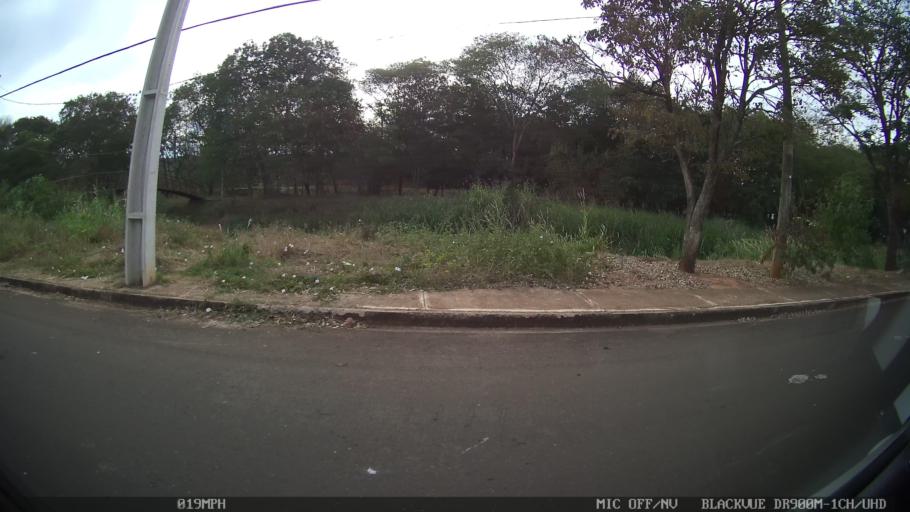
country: BR
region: Sao Paulo
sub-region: Catanduva
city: Catanduva
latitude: -21.1240
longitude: -48.9817
